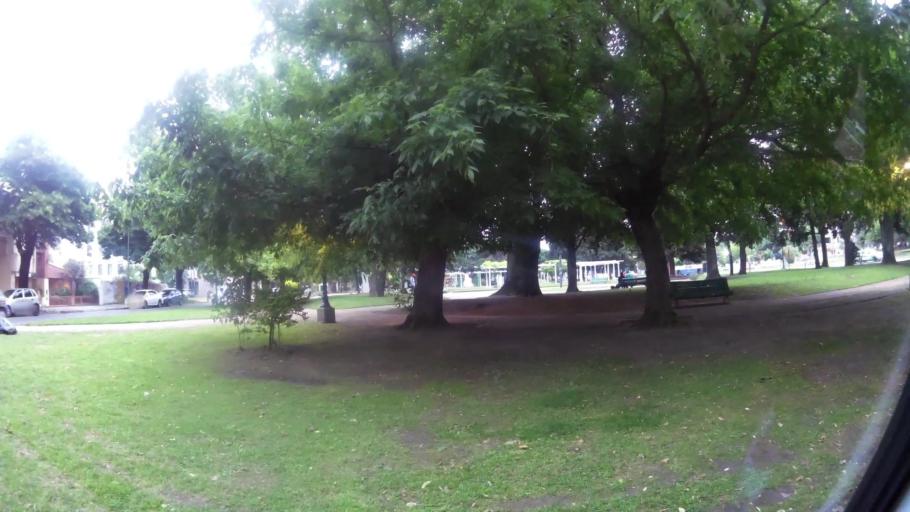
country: AR
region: Buenos Aires
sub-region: Partido de La Plata
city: La Plata
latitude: -34.9063
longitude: -57.9620
